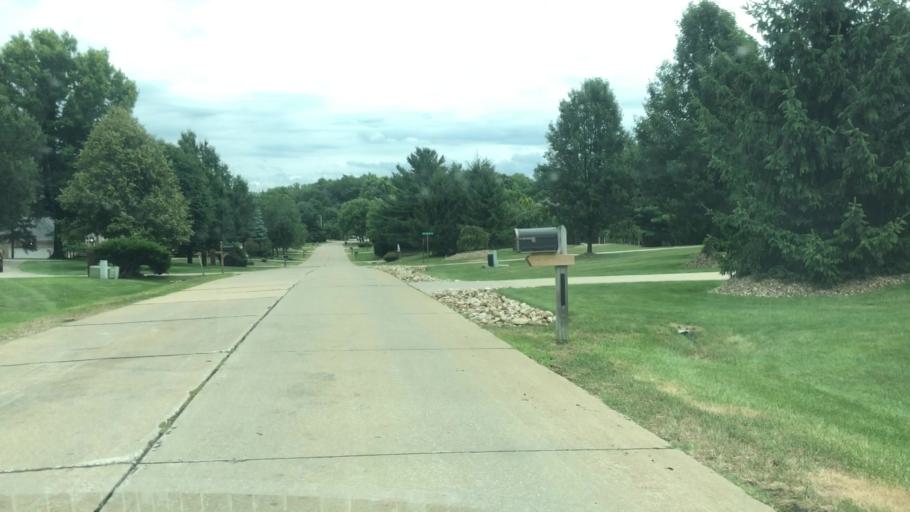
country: US
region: Ohio
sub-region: Summit County
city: Montrose-Ghent
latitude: 41.1532
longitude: -81.6419
